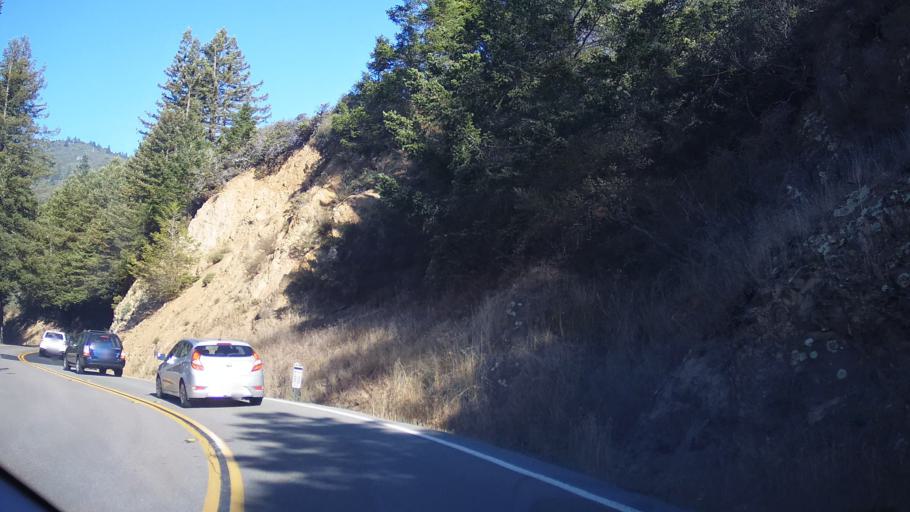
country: US
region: California
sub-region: Marin County
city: Mill Valley
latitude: 37.9119
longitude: -122.5791
